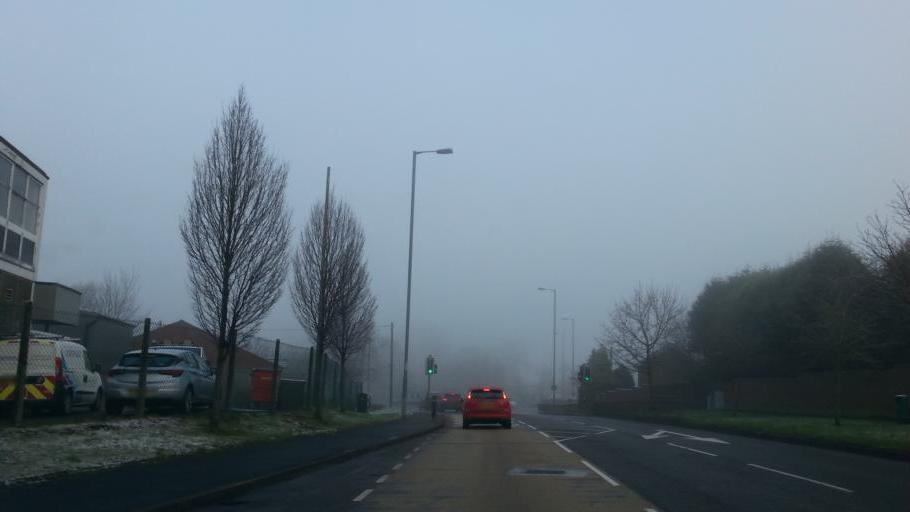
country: GB
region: England
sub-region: Staffordshire
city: Biddulph
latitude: 53.1155
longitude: -2.1795
